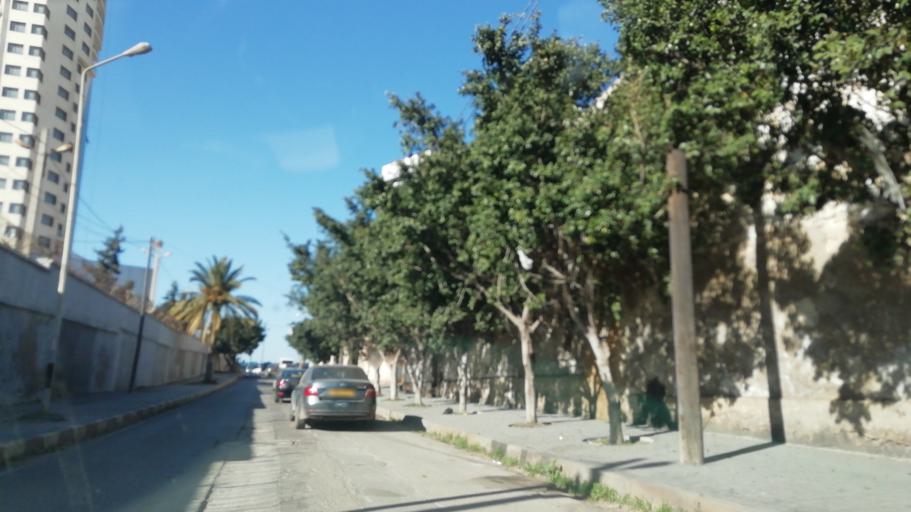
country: DZ
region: Oran
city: Oran
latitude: 35.7110
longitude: -0.6228
